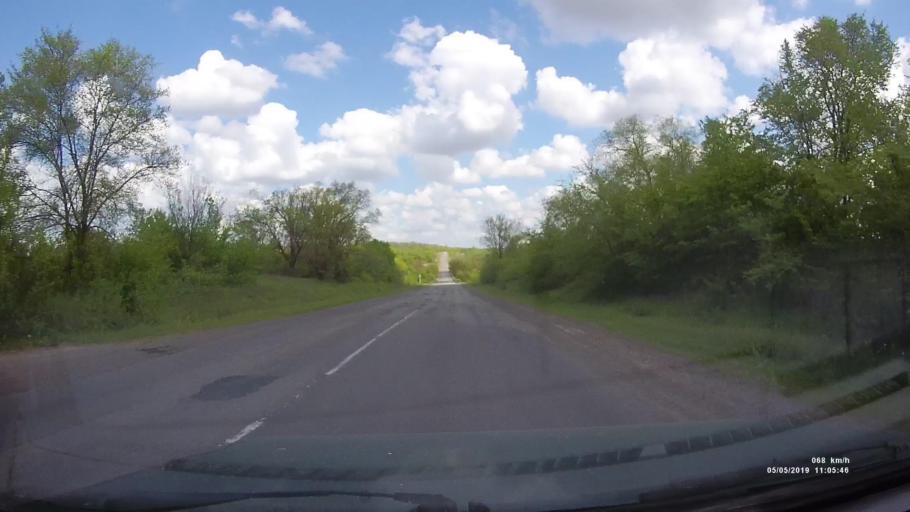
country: RU
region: Rostov
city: Ust'-Donetskiy
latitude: 47.7091
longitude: 40.9113
